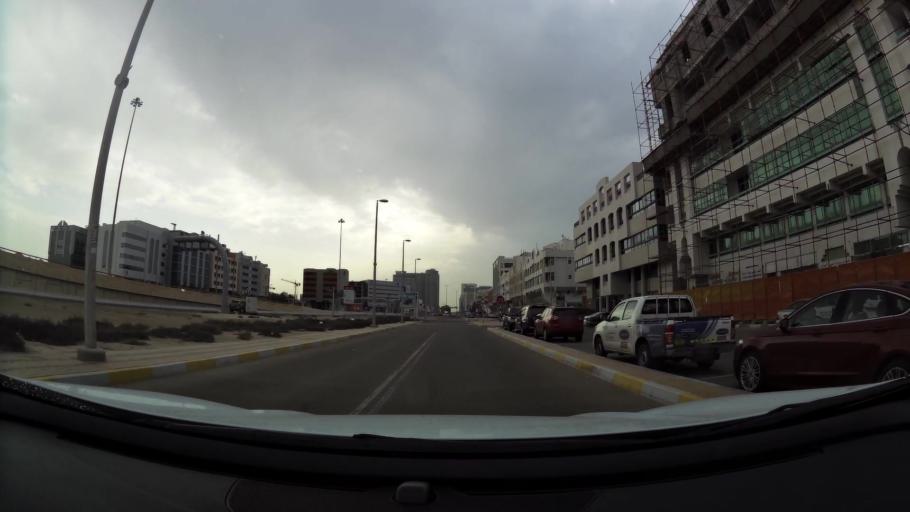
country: AE
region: Abu Dhabi
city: Abu Dhabi
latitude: 24.4800
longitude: 54.3843
